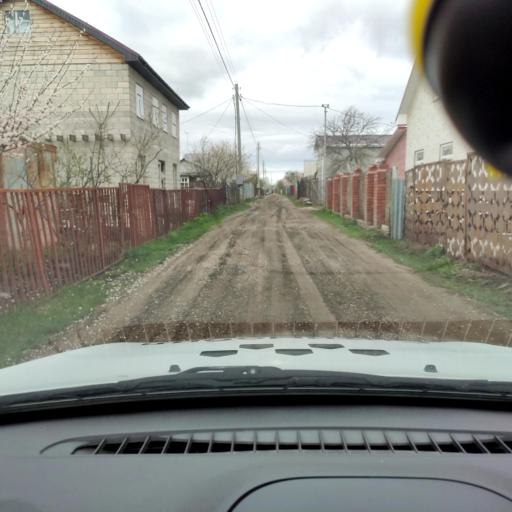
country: RU
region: Samara
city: Tol'yatti
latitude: 53.5824
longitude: 49.3157
